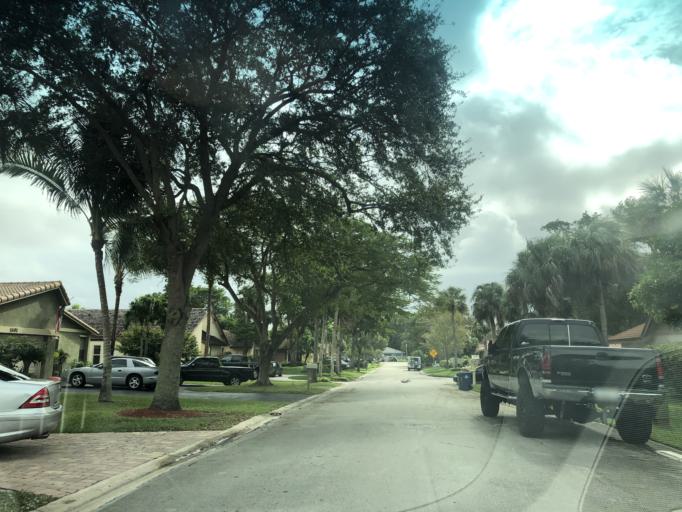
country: US
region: Florida
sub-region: Broward County
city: Margate
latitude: 26.2506
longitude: -80.2347
